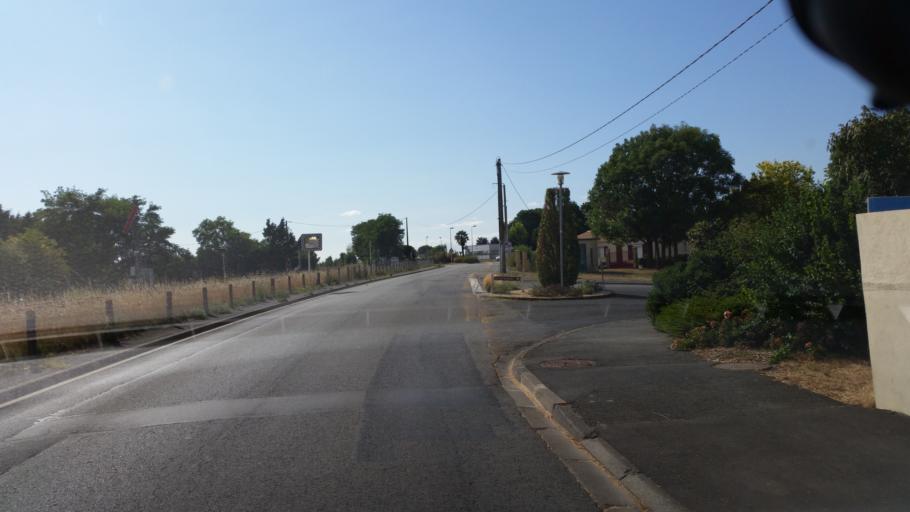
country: FR
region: Poitou-Charentes
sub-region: Departement de la Charente-Maritime
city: Marans
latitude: 46.3053
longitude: -1.0040
